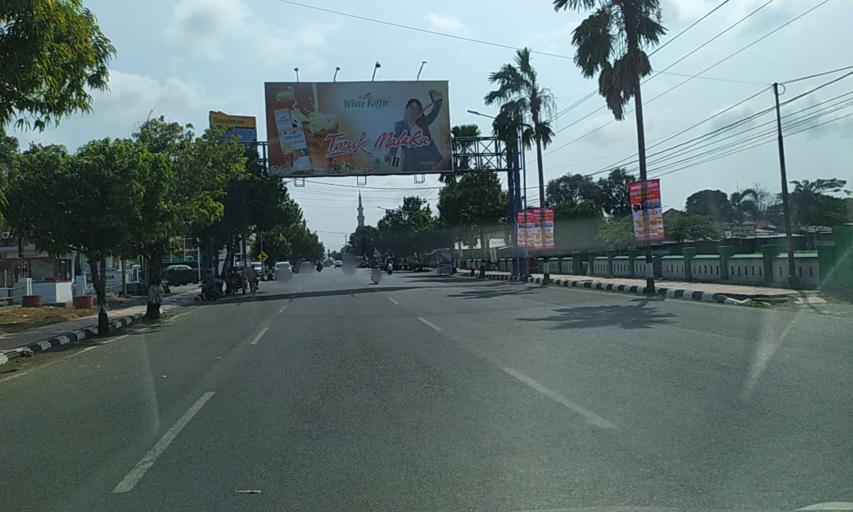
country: ID
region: Central Java
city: Karangbadar Kidul
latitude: -7.7279
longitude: 109.0124
